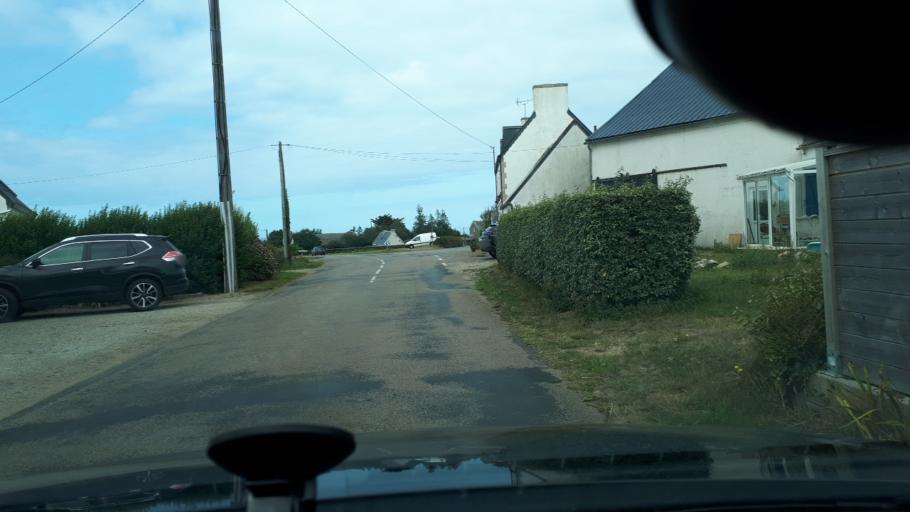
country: FR
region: Brittany
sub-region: Departement du Finistere
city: Plozevet
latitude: 47.9588
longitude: -4.3973
